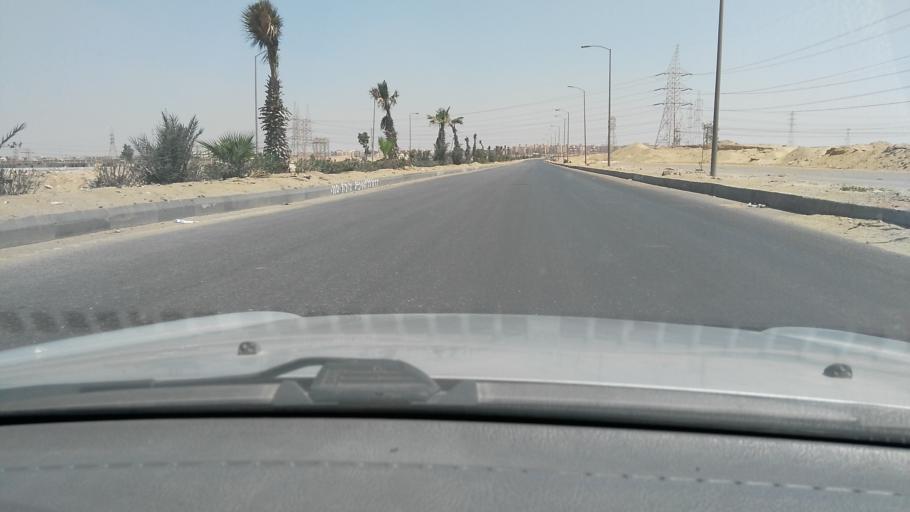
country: EG
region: Al Jizah
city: Madinat Sittah Uktubar
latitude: 29.9418
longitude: 30.9480
